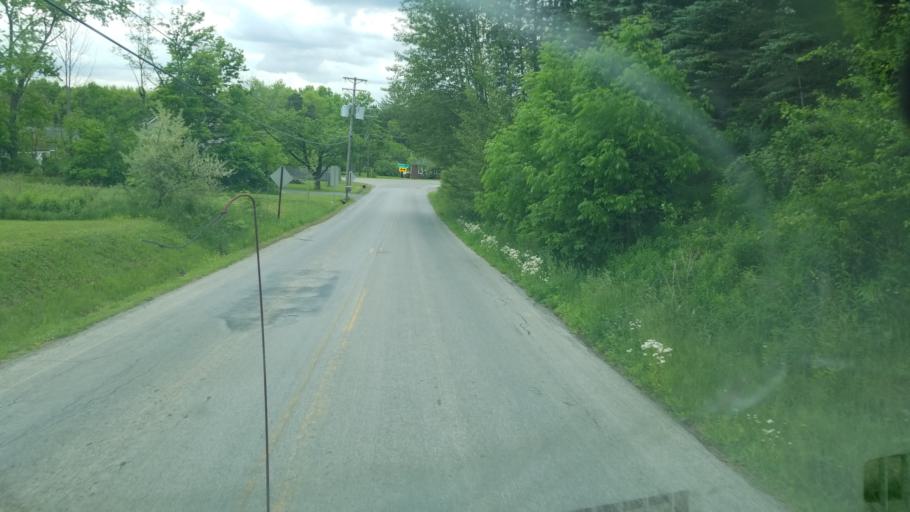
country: US
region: Pennsylvania
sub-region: Venango County
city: Franklin
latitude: 41.2011
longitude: -79.8443
